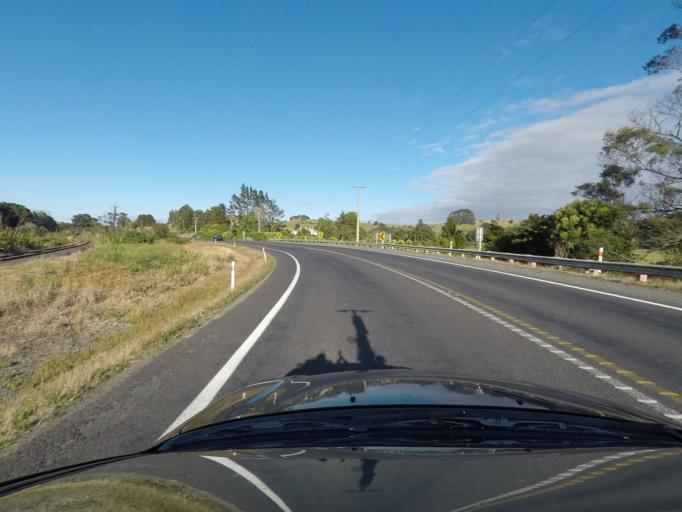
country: NZ
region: Northland
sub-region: Far North District
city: Kawakawa
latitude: -35.4949
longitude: 174.1530
